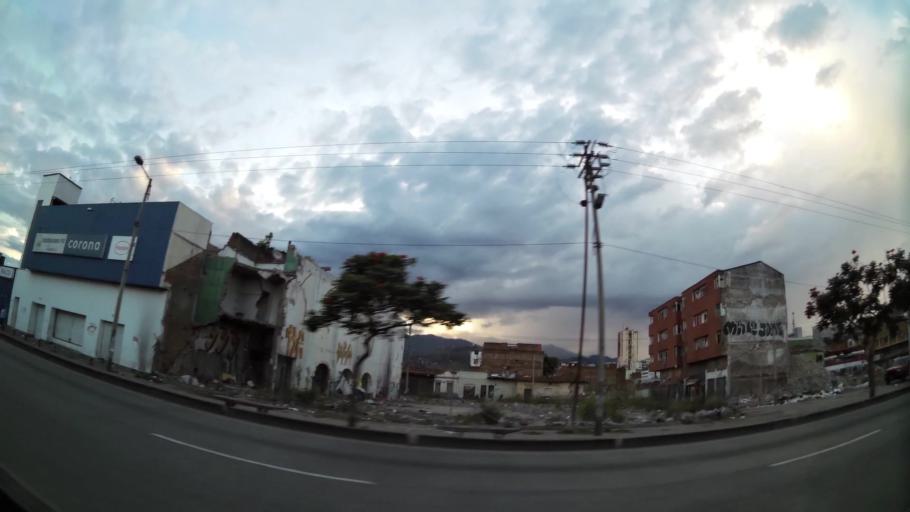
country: CO
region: Valle del Cauca
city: Cali
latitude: 3.4464
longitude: -76.5283
